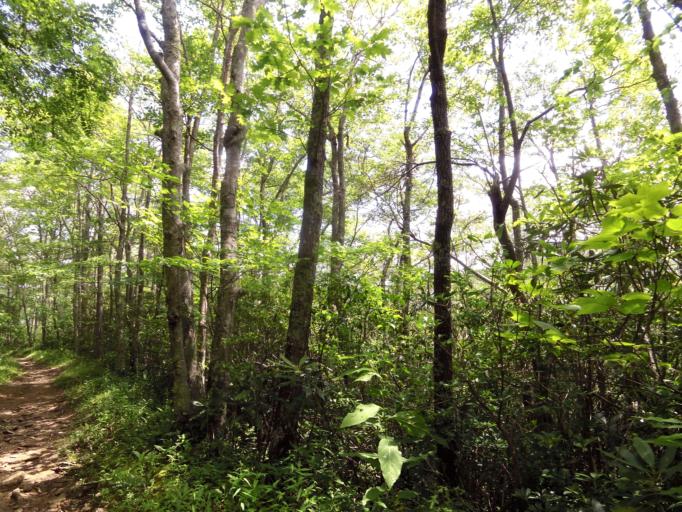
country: US
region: Tennessee
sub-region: Sevier County
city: Gatlinburg
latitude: 35.5866
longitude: -83.7336
